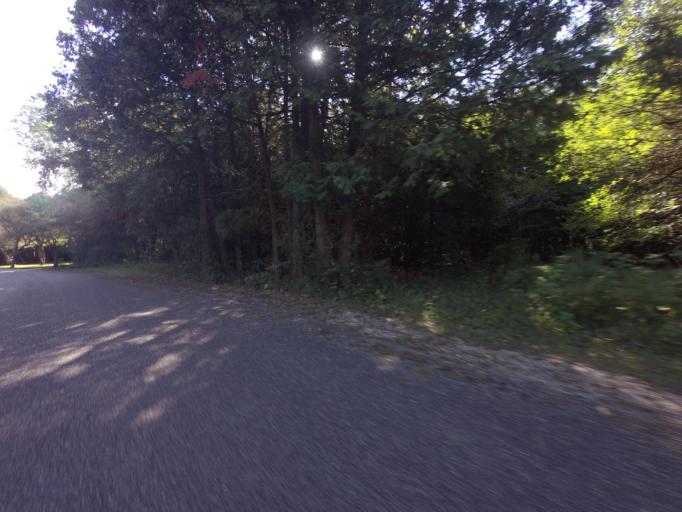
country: CA
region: Ontario
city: Waterloo
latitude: 43.6735
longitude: -80.4508
